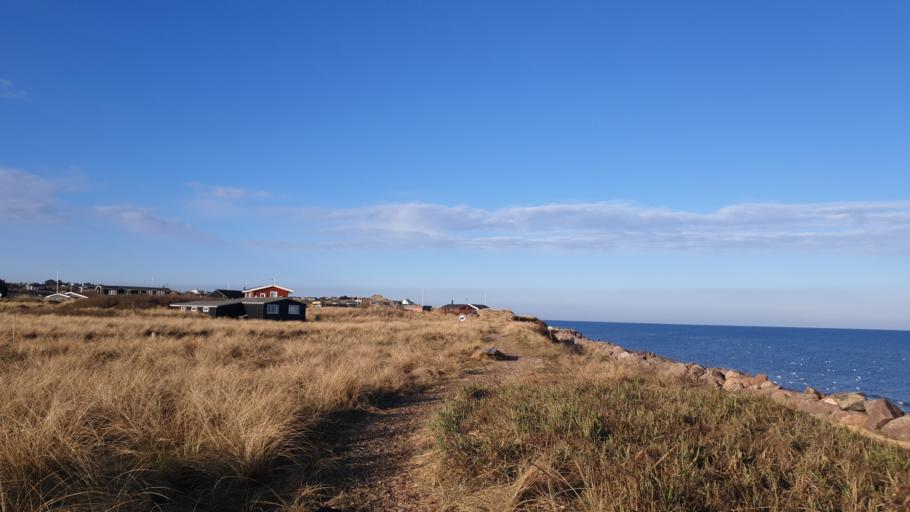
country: DK
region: North Denmark
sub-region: Hjorring Kommune
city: Hjorring
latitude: 57.4875
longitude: 9.8163
